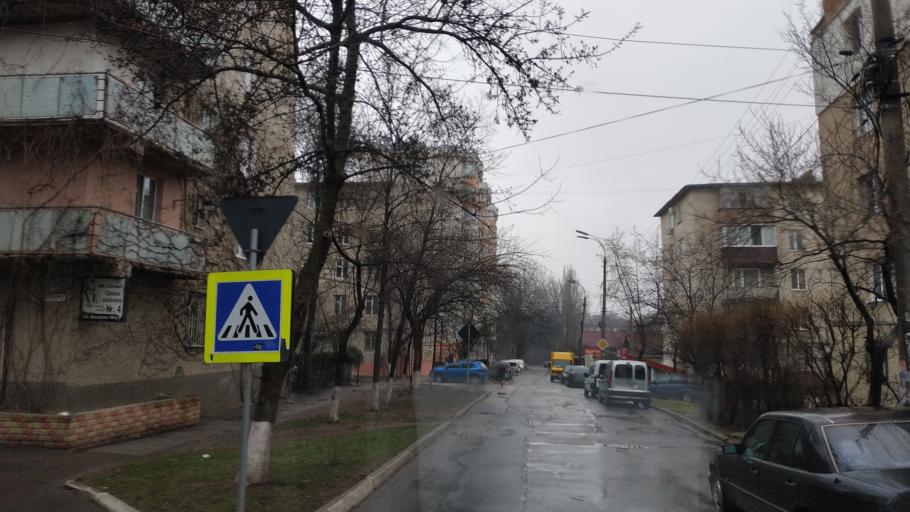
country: MD
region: Chisinau
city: Vatra
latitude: 47.0356
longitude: 28.7811
